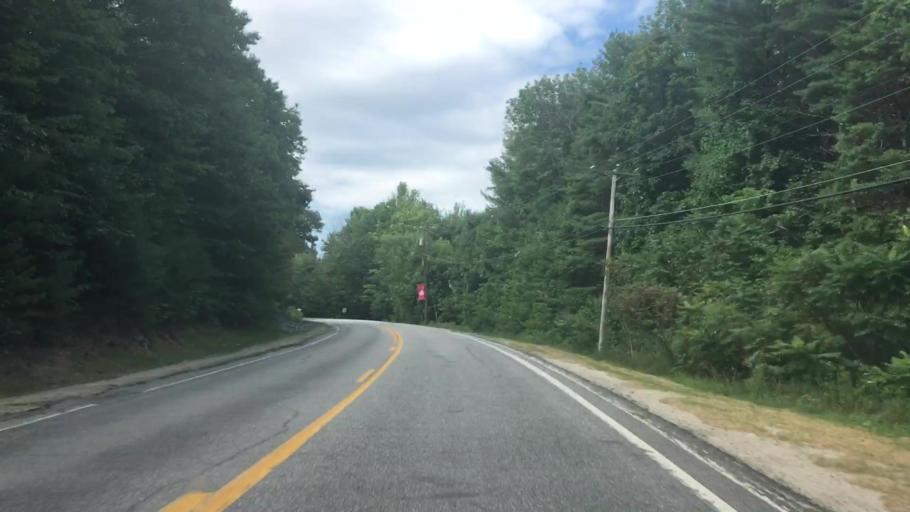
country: US
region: Maine
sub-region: Cumberland County
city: Raymond
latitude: 43.9998
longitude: -70.5193
